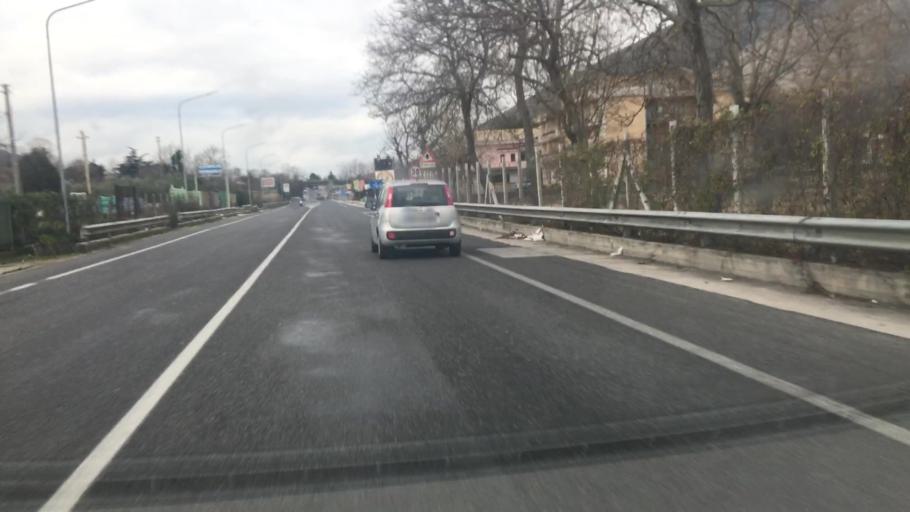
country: IT
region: Campania
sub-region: Provincia di Benevento
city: Arpaia
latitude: 41.0411
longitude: 14.5638
